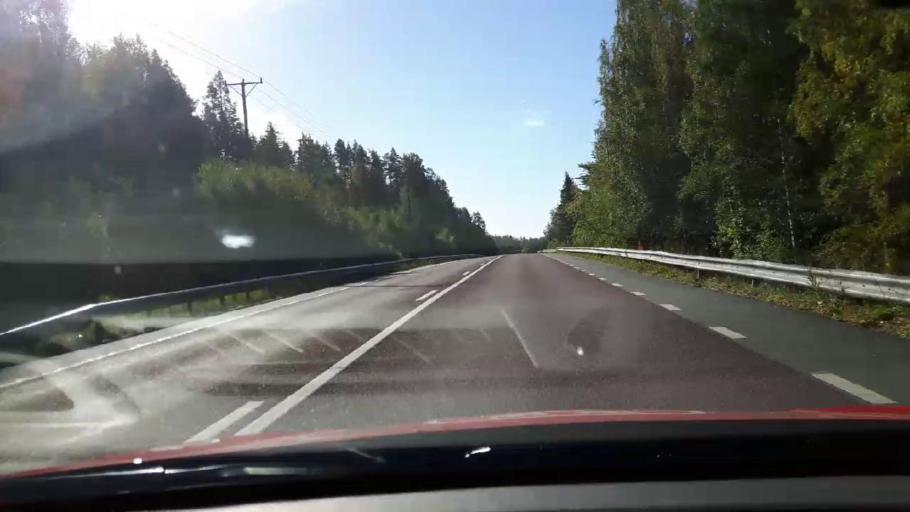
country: SE
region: Jaemtland
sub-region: Braecke Kommun
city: Braecke
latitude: 62.7921
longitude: 15.3765
